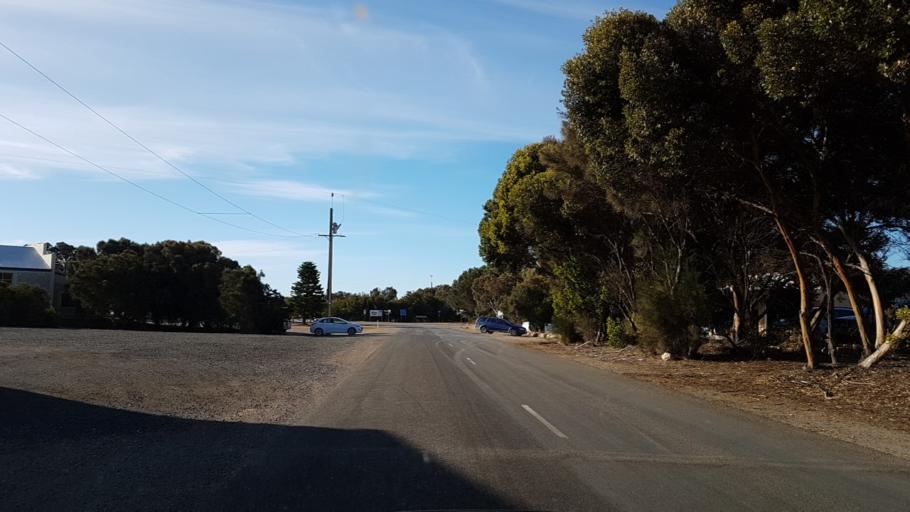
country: AU
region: South Australia
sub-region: Yorke Peninsula
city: Port Victoria
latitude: -34.9264
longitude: 137.0841
